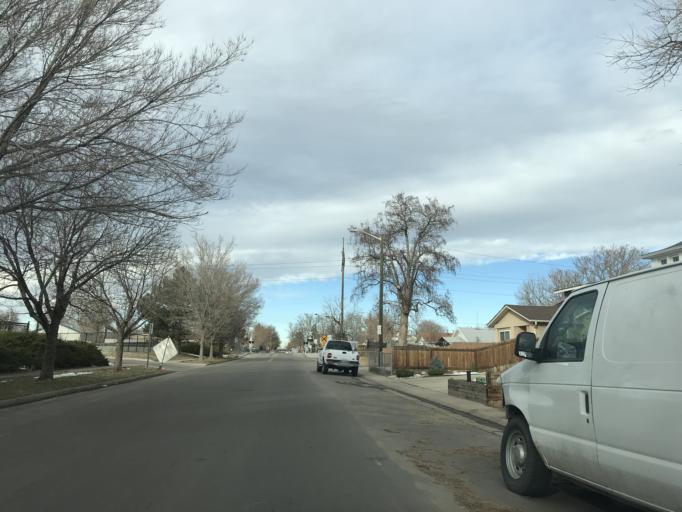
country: US
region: Colorado
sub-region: Adams County
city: Commerce City
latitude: 39.7742
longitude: -104.9542
